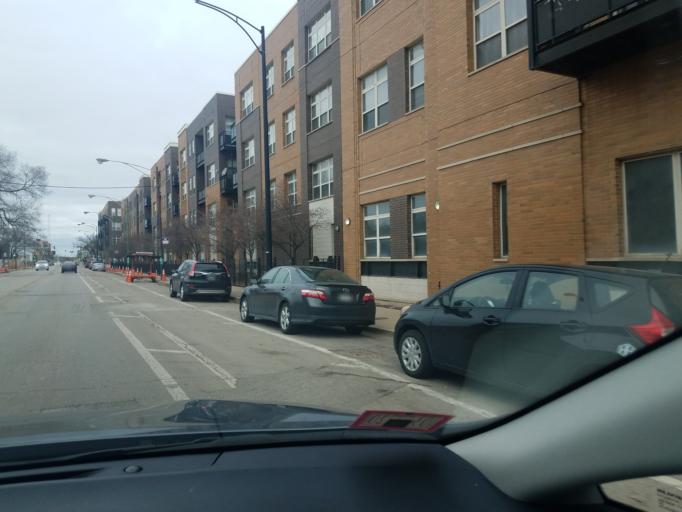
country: US
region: Illinois
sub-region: Cook County
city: Lincolnwood
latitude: 41.9346
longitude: -87.6813
